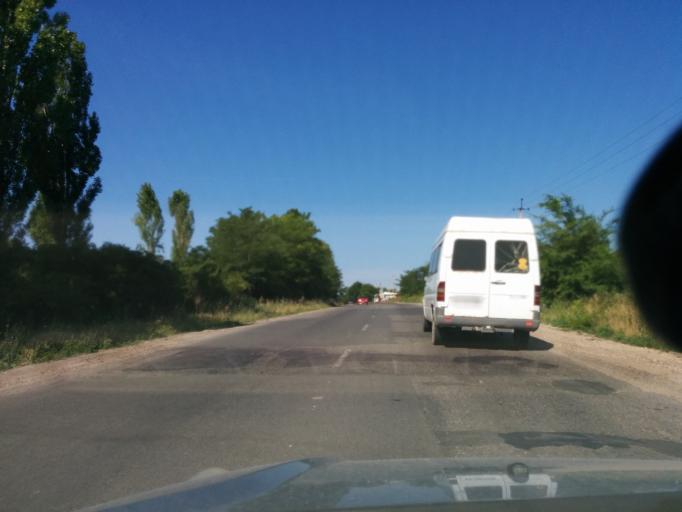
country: MD
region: Chisinau
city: Ciorescu
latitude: 47.0623
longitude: 28.9583
